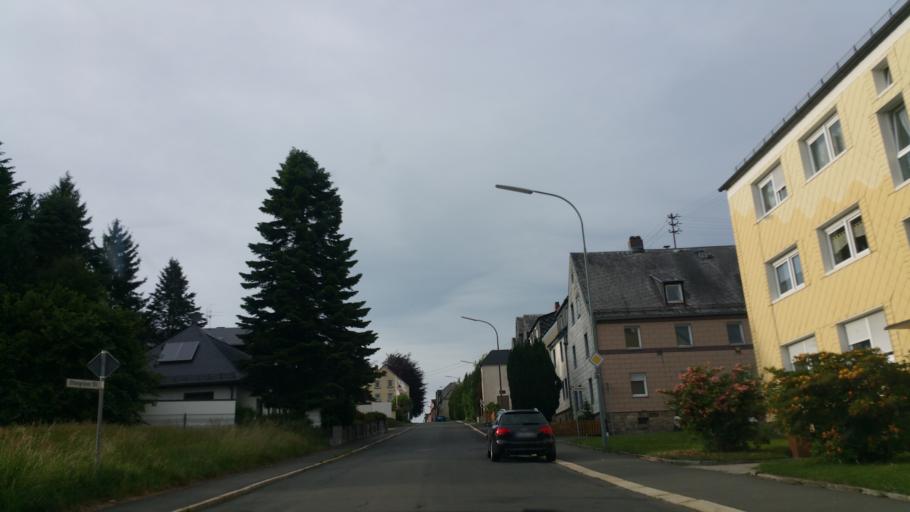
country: DE
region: Bavaria
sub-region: Upper Franconia
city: Helmbrechts
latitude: 50.2326
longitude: 11.7171
